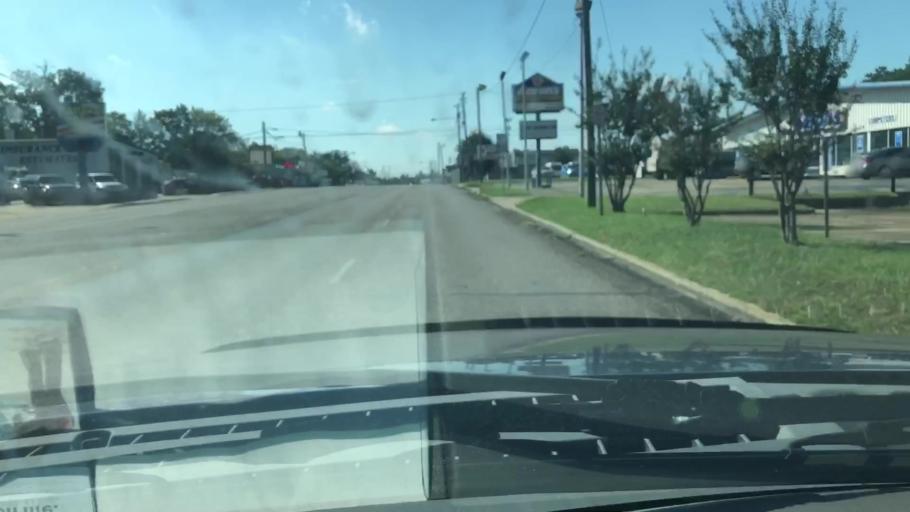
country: US
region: Texas
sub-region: Bowie County
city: Texarkana
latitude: 33.4395
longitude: -94.0533
